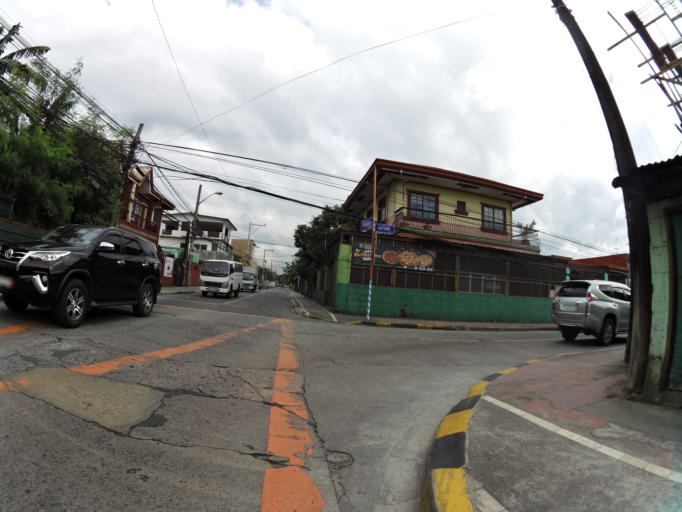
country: PH
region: Calabarzon
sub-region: Province of Rizal
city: Antipolo
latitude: 14.6433
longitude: 121.1093
